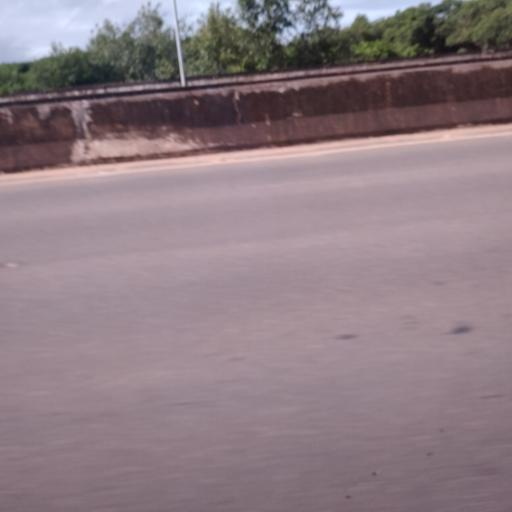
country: BR
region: Maranhao
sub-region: Sao Luis
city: Sao Luis
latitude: -2.5128
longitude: -44.2710
